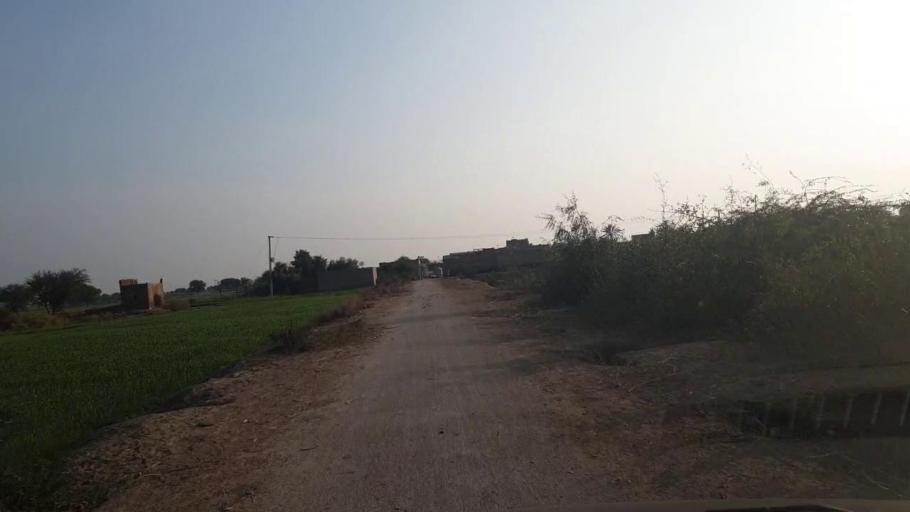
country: PK
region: Sindh
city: Tando Adam
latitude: 25.8562
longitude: 68.7137
